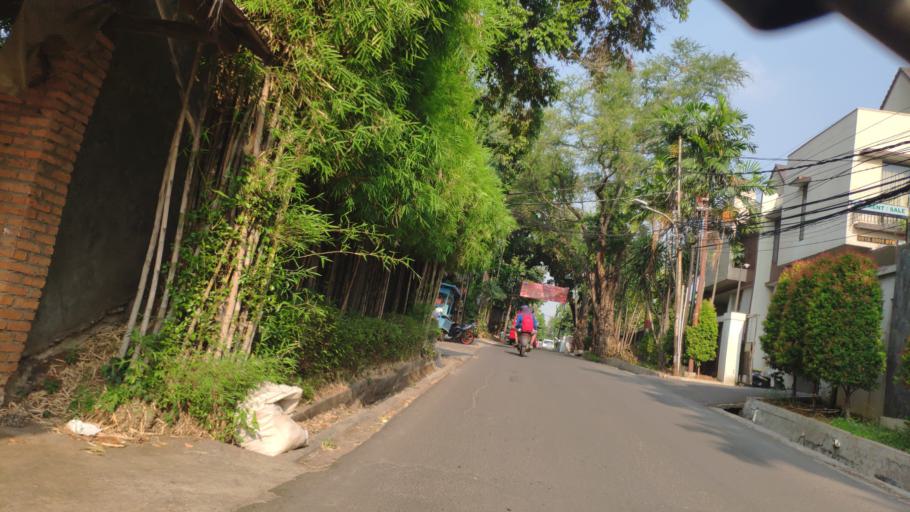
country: ID
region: Banten
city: South Tangerang
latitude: -6.2872
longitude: 106.8010
